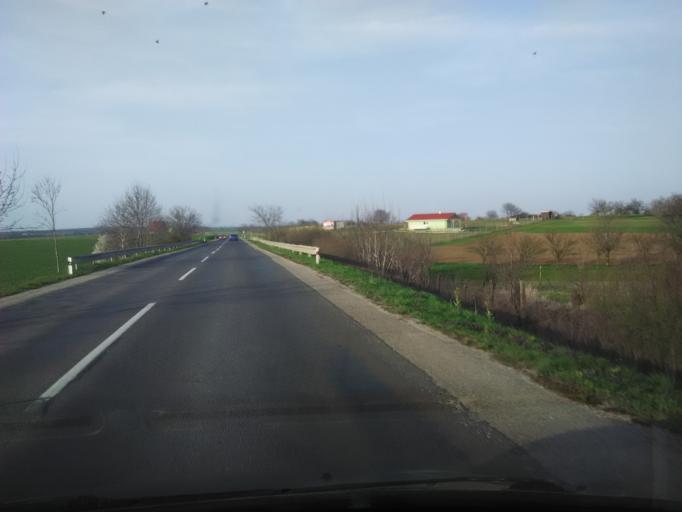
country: SK
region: Nitriansky
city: Surany
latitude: 48.0933
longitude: 18.2917
